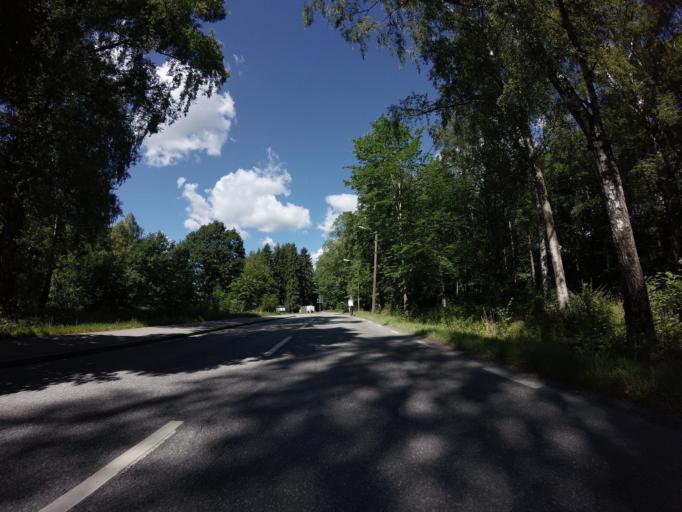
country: SE
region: Stockholm
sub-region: Lidingo
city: Lidingoe
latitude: 59.3334
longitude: 18.1265
